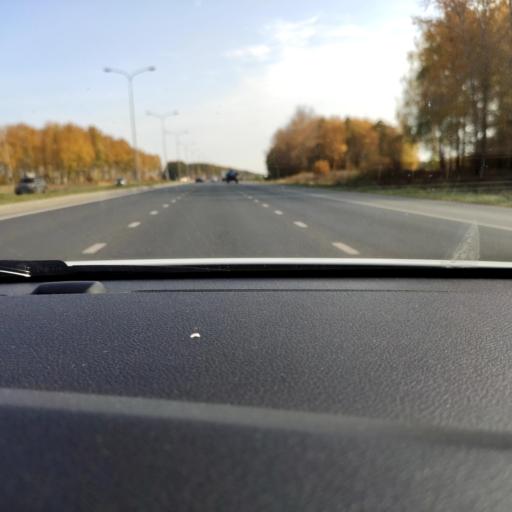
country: RU
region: Tatarstan
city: Vysokaya Gora
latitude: 55.8010
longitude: 49.3150
